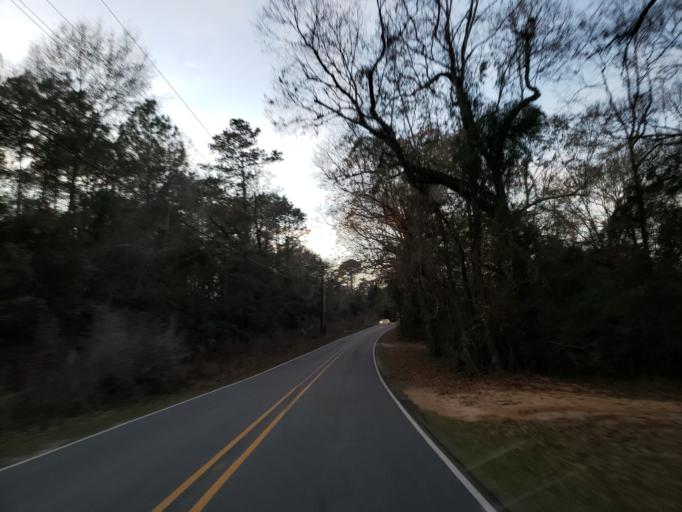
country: US
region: Mississippi
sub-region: Lamar County
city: West Hattiesburg
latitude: 31.2511
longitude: -89.3336
